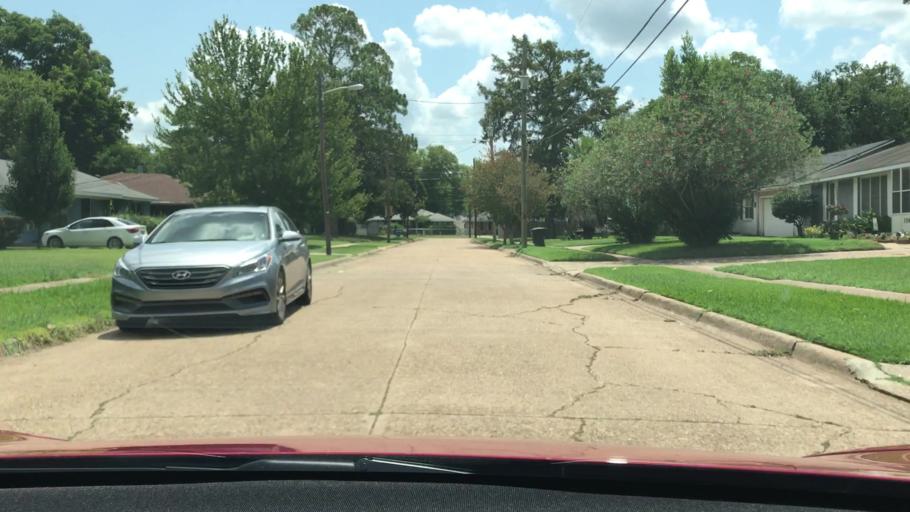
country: US
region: Louisiana
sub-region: Bossier Parish
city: Bossier City
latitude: 32.4573
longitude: -93.7273
